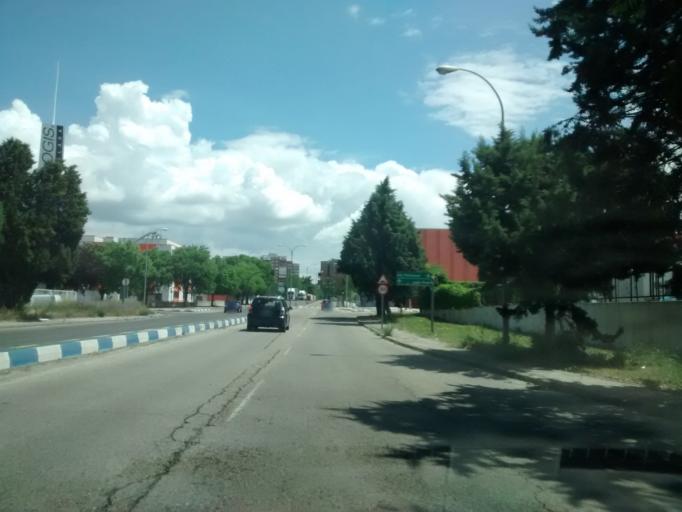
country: ES
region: Madrid
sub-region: Provincia de Madrid
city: Coslada
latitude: 40.4314
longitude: -3.5531
